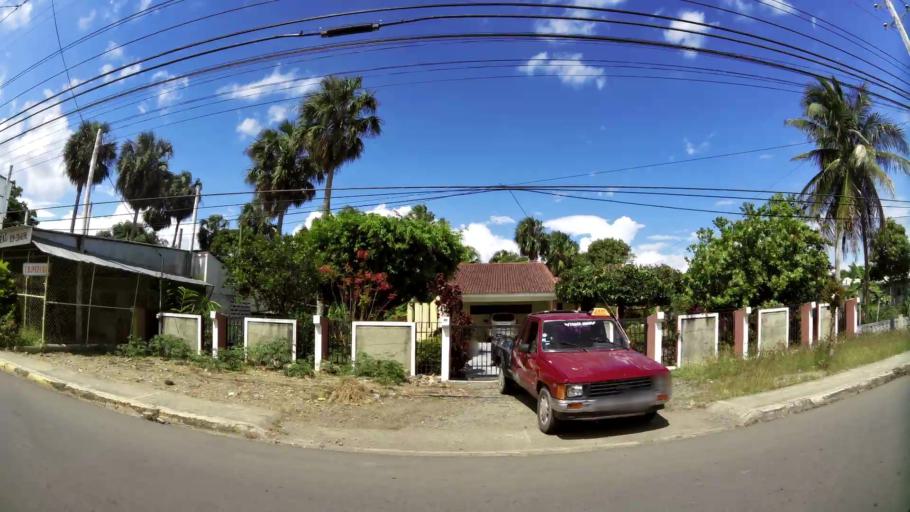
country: DO
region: Santiago
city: Licey al Medio
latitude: 19.3849
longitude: -70.6263
